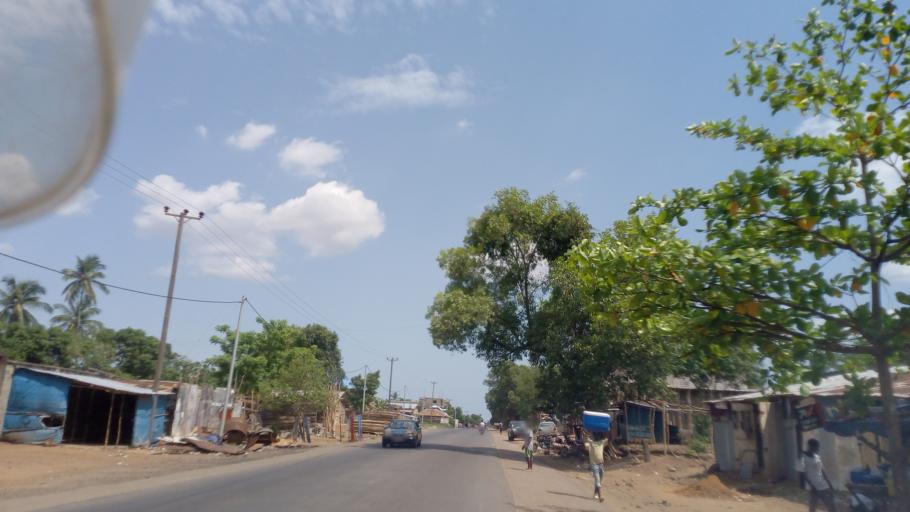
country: SL
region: Western Area
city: Waterloo
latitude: 8.3190
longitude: -13.0728
